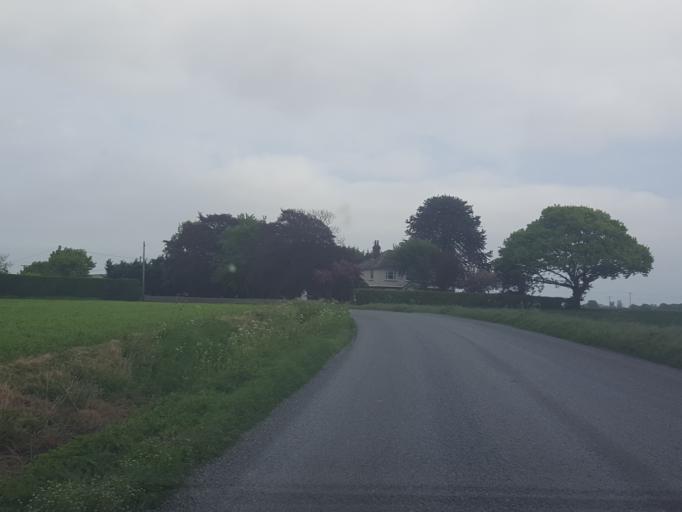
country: GB
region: England
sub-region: Essex
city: Frinton-on-Sea
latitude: 51.8528
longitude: 1.1976
